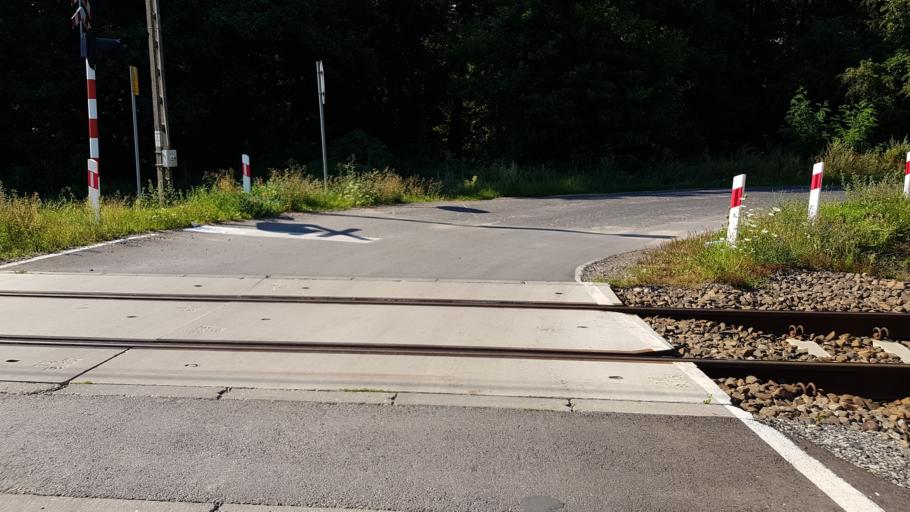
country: PL
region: West Pomeranian Voivodeship
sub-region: Powiat gryfinski
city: Widuchowa
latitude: 53.1641
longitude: 14.4651
